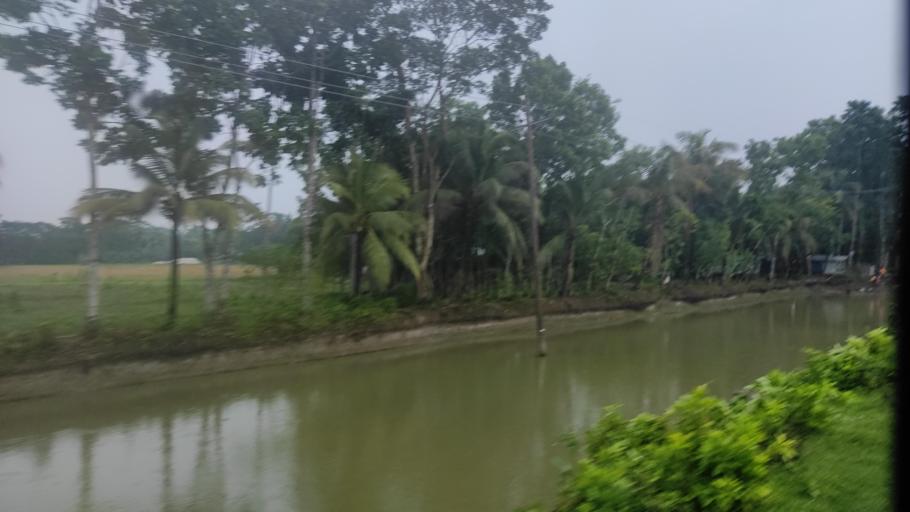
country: BD
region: Barisal
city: Bhandaria
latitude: 22.3049
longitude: 90.3246
